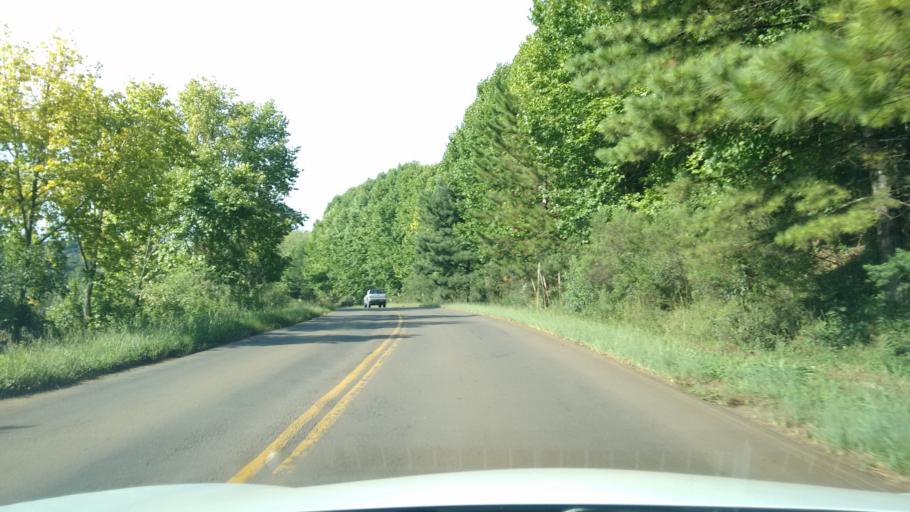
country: BR
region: Santa Catarina
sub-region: Videira
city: Videira
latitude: -27.1031
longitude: -50.9141
